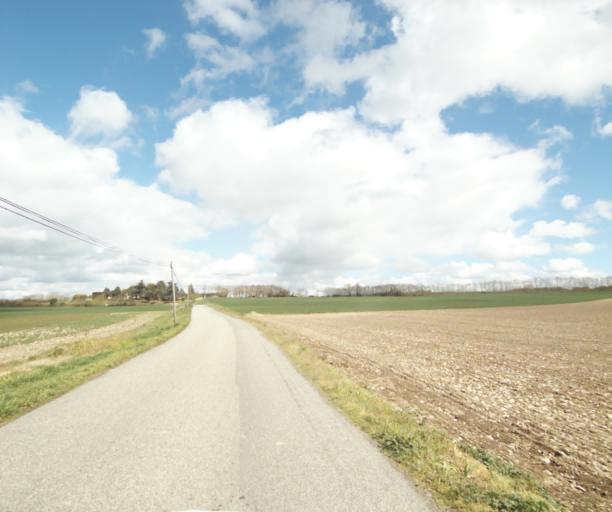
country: FR
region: Midi-Pyrenees
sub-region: Departement de l'Ariege
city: Saverdun
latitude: 43.2429
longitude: 1.5872
